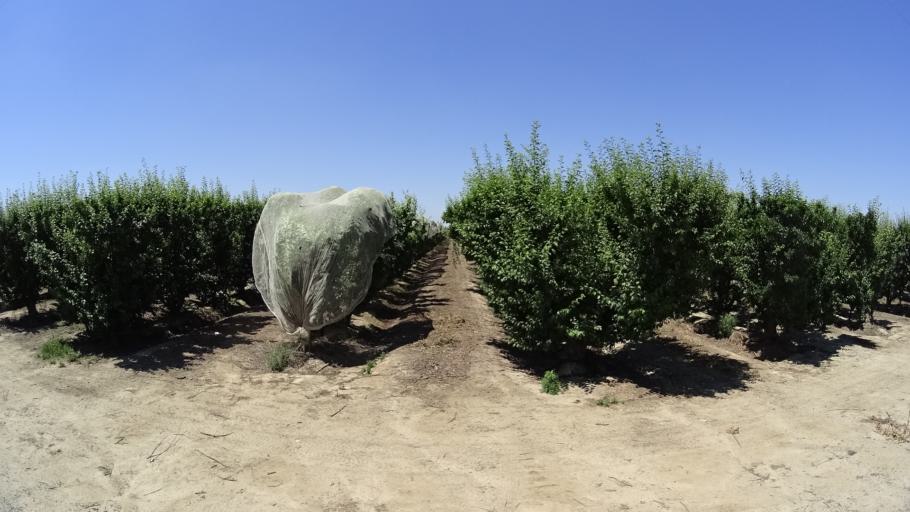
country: US
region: California
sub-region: Fresno County
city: Kingsburg
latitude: 36.4789
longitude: -119.5911
